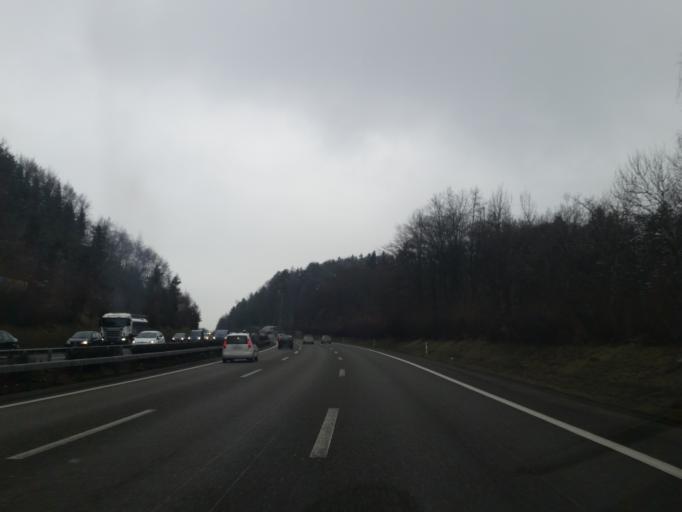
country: CH
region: Zurich
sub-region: Bezirk Pfaeffikon
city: Tagelswangen
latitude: 47.4276
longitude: 8.6781
